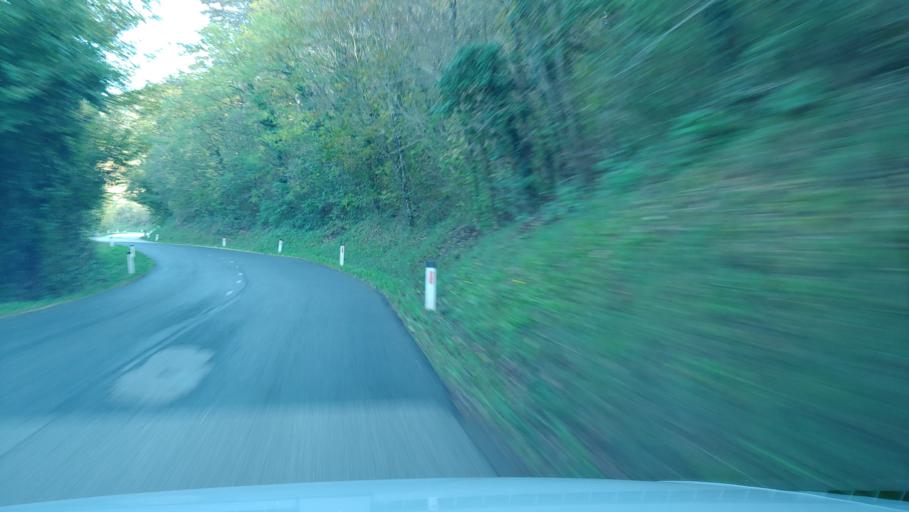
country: SI
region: Vipava
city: Vipava
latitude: 45.8127
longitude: 13.9085
